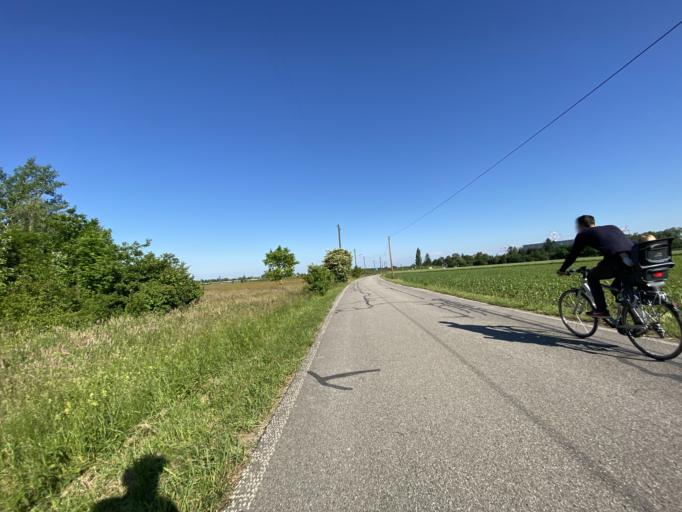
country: DE
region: Bavaria
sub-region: Upper Bavaria
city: Pasing
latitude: 48.1717
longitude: 11.4322
